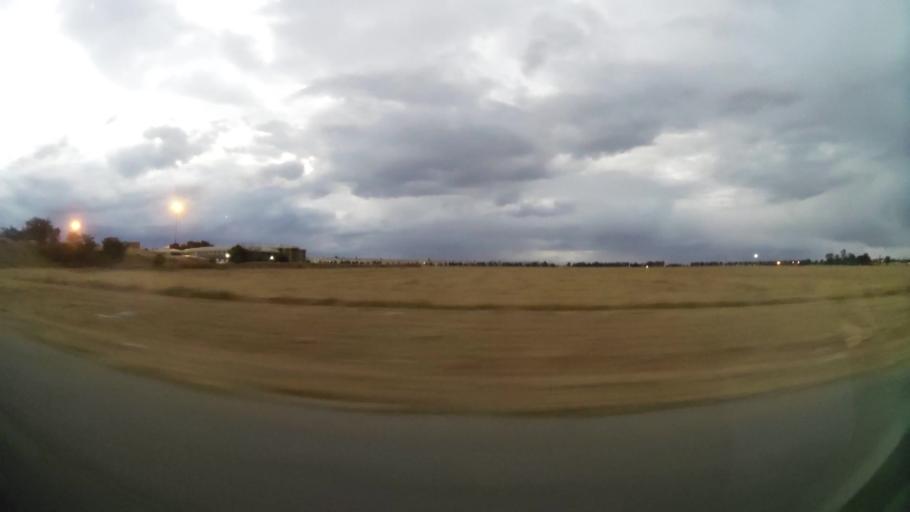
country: ZA
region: Orange Free State
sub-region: Lejweleputswa District Municipality
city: Welkom
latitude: -27.9517
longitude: 26.7915
